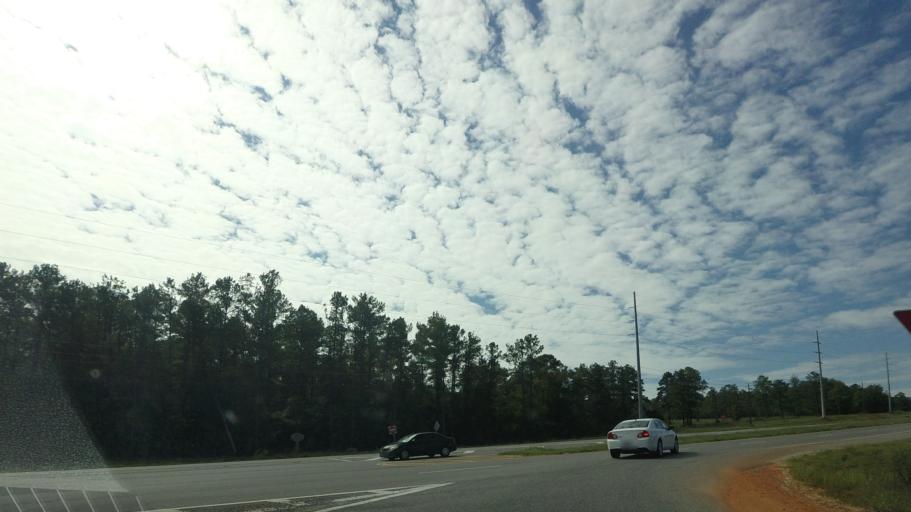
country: US
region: Georgia
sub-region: Houston County
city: Centerville
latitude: 32.6809
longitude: -83.7010
